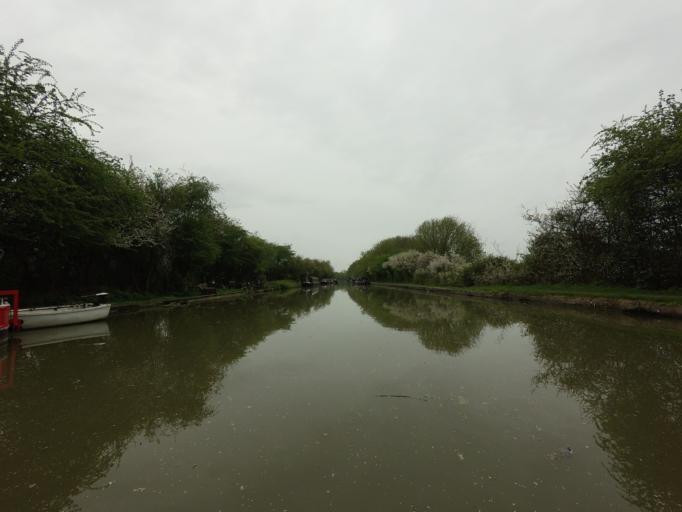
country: GB
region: England
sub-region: Milton Keynes
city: Stony Stratford
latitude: 52.0696
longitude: -0.8352
